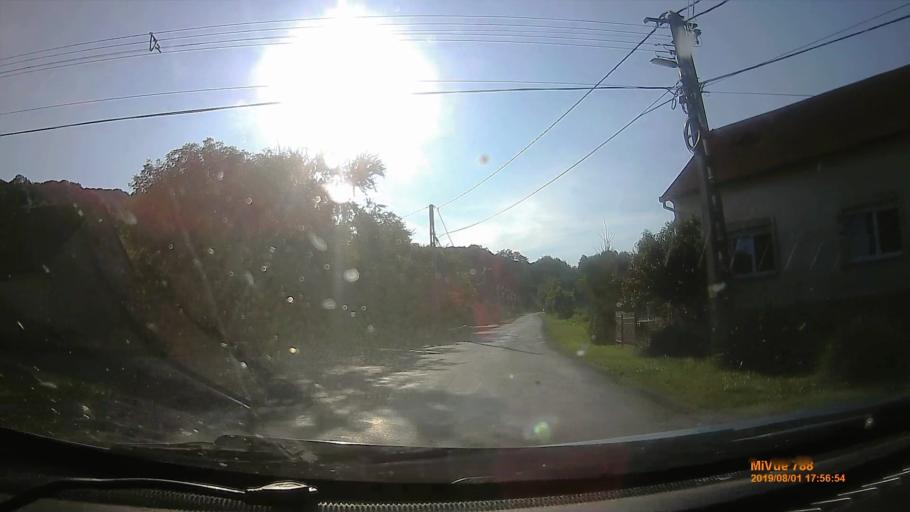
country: HU
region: Baranya
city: Sasd
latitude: 46.1983
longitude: 18.1184
